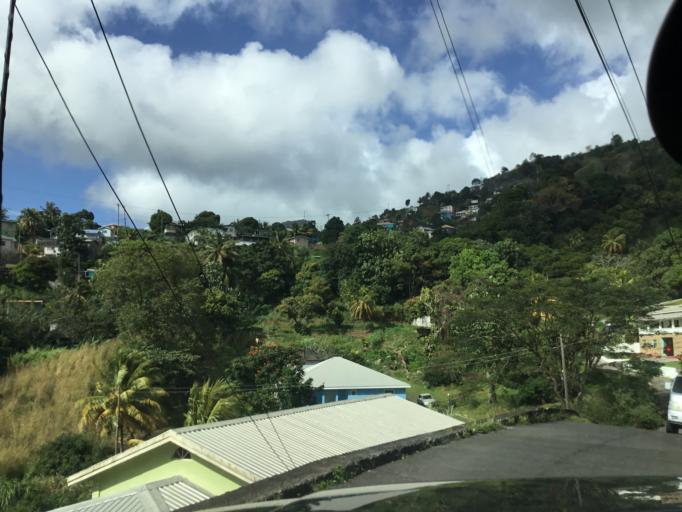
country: VC
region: Saint George
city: Kingstown
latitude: 13.1630
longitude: -61.2173
